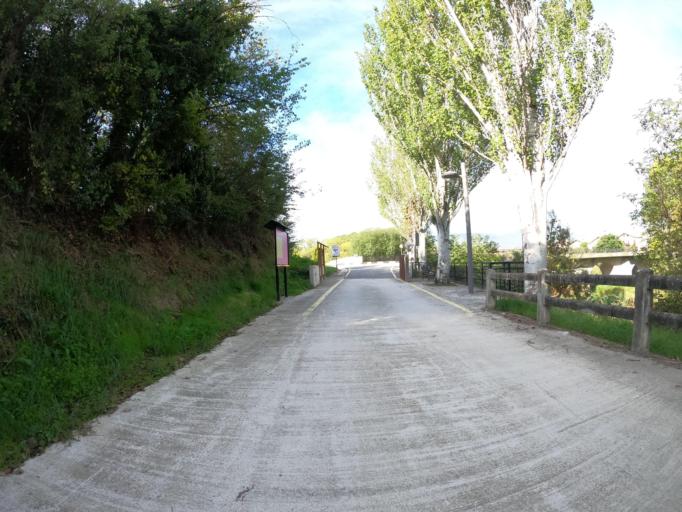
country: ES
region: Navarre
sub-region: Provincia de Navarra
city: Oltza
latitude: 42.8142
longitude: -1.7476
